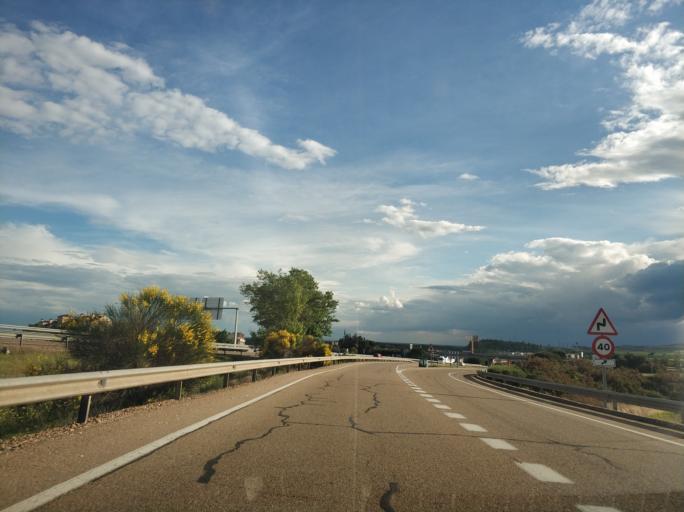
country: ES
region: Castille and Leon
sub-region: Provincia de Valladolid
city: Arroyo
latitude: 41.6149
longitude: -4.7930
